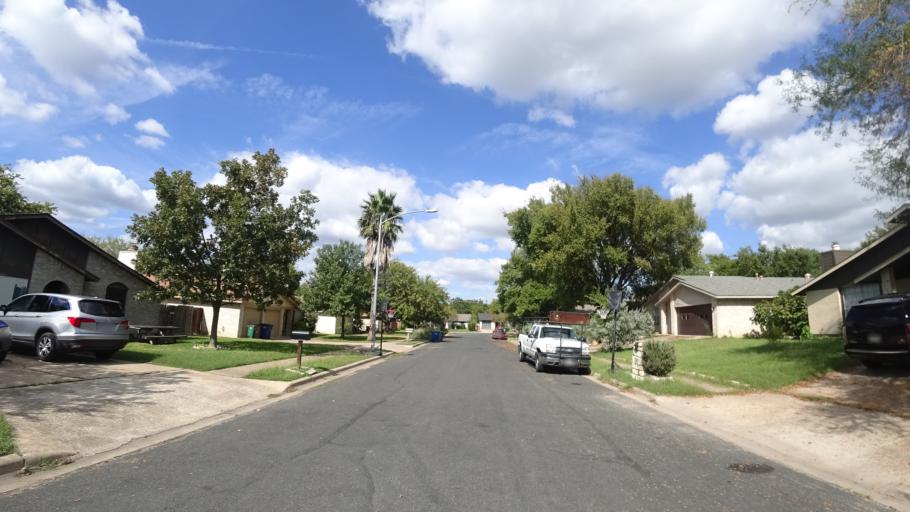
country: US
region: Texas
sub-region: Travis County
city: Onion Creek
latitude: 30.2051
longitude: -97.7968
